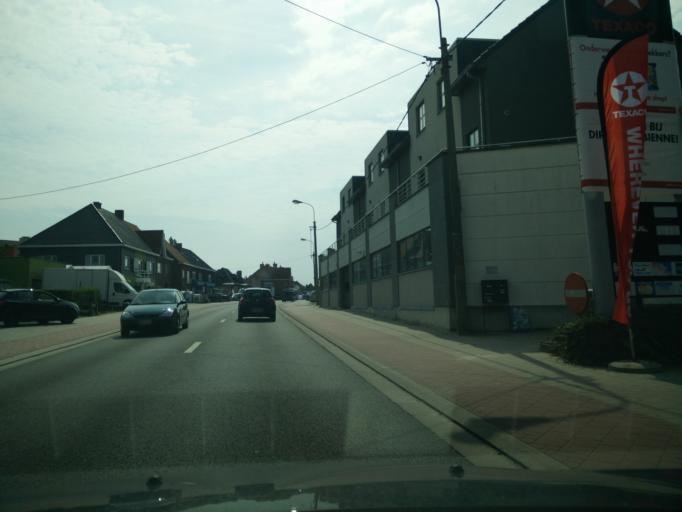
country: BE
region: Flanders
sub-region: Provincie Oost-Vlaanderen
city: Merelbeke
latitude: 50.9886
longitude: 3.7463
